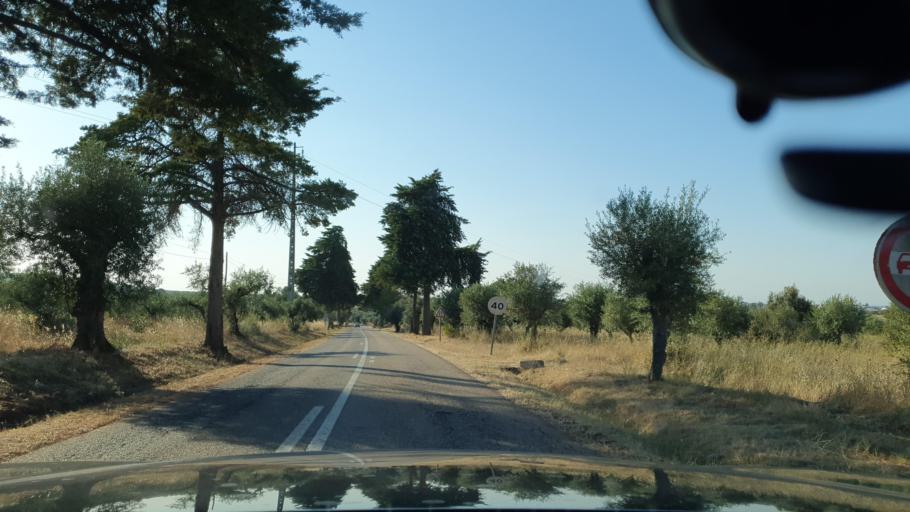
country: PT
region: Portalegre
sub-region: Fronteira
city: Fronteira
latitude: 38.9365
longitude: -7.6698
